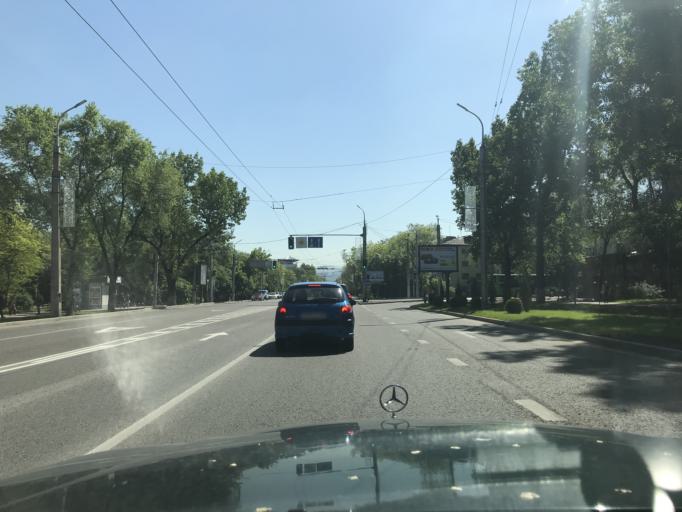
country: KZ
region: Almaty Qalasy
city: Almaty
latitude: 43.2251
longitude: 76.8954
